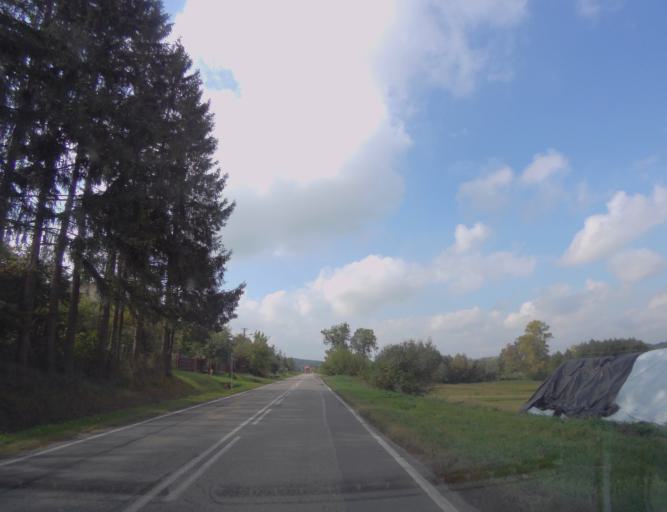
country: PL
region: Lublin Voivodeship
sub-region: Powiat krasnostawski
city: Krasnystaw
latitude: 50.9687
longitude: 23.1257
